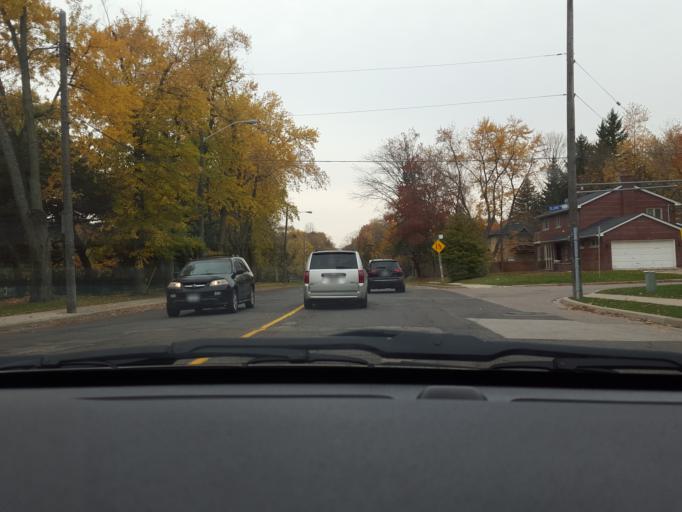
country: CA
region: Ontario
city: Willowdale
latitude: 43.7347
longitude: -79.3591
